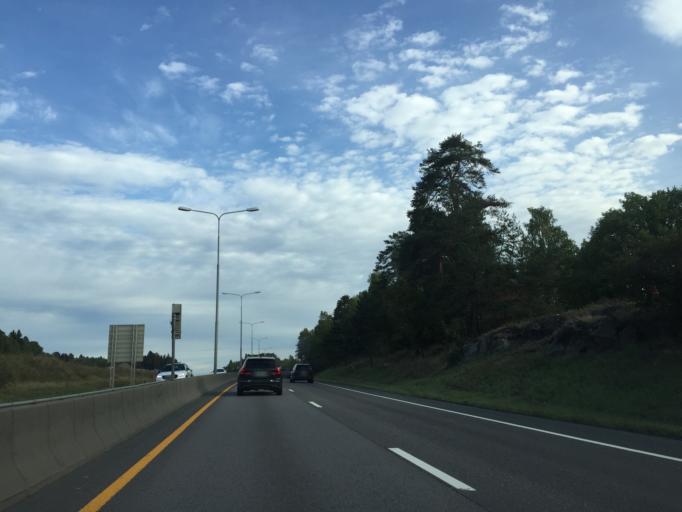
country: NO
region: Akershus
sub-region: Oppegard
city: Kolbotn
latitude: 59.8455
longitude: 10.8372
